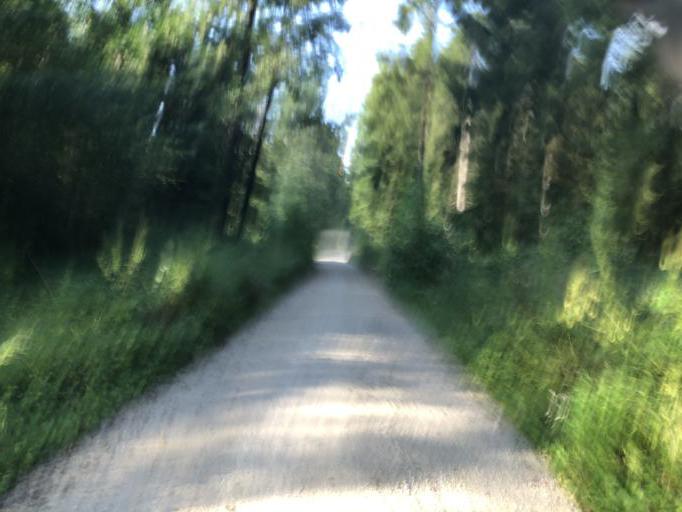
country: DE
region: Bavaria
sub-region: Regierungsbezirk Mittelfranken
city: Buckenhof
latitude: 49.5499
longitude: 11.0448
